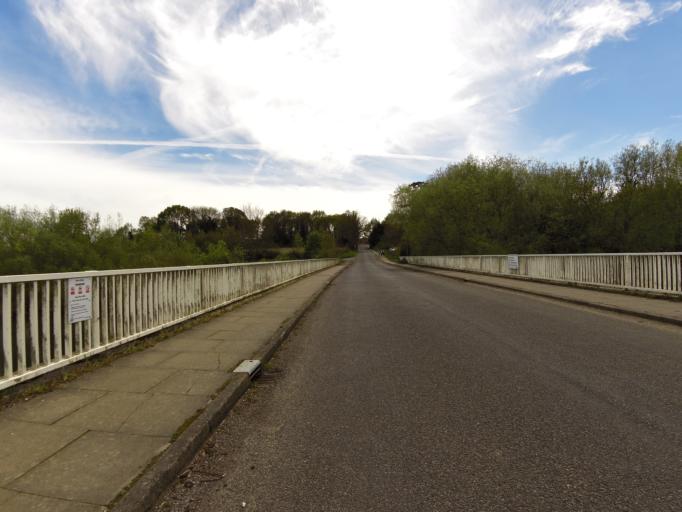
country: GB
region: England
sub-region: Essex
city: Mistley
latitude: 51.9947
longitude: 1.1110
